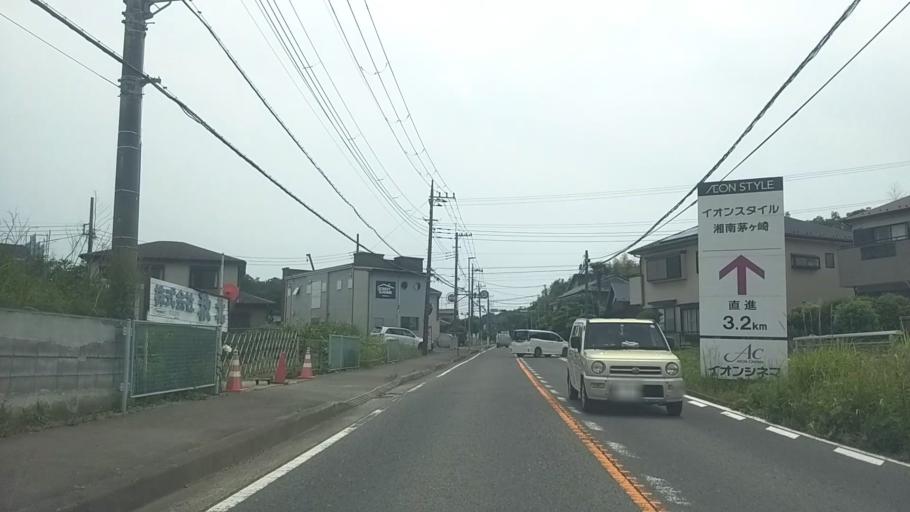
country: JP
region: Kanagawa
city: Chigasaki
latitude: 35.3620
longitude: 139.4219
